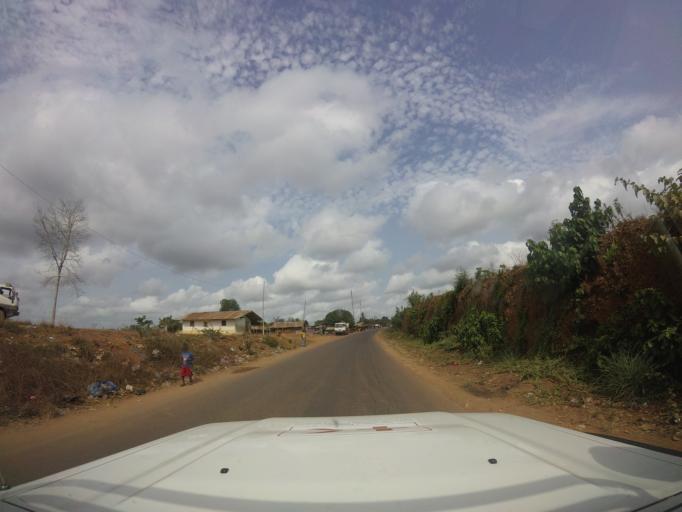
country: LR
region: Bomi
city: Tubmanburg
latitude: 6.7129
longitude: -10.9691
